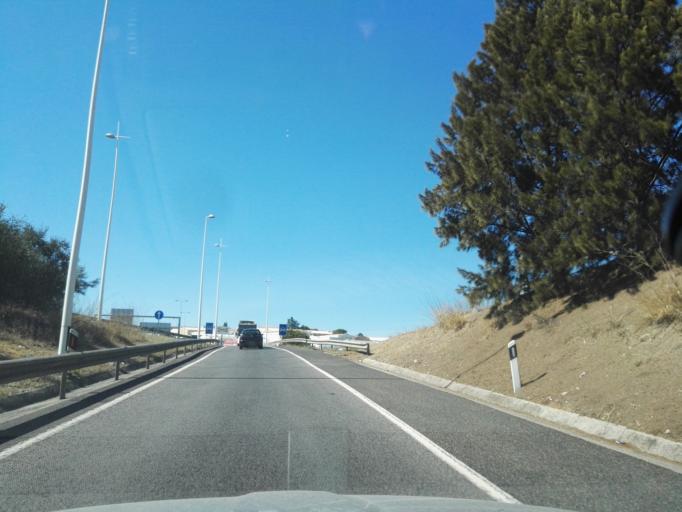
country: PT
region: Lisbon
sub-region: Loures
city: Sacavem
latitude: 38.7936
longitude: -9.1158
